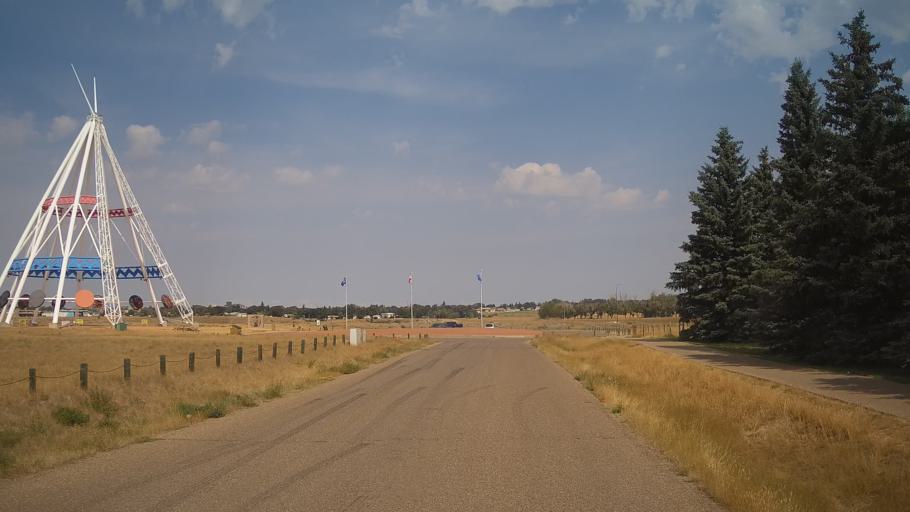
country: CA
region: Alberta
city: Medicine Hat
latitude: 50.0139
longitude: -110.6905
